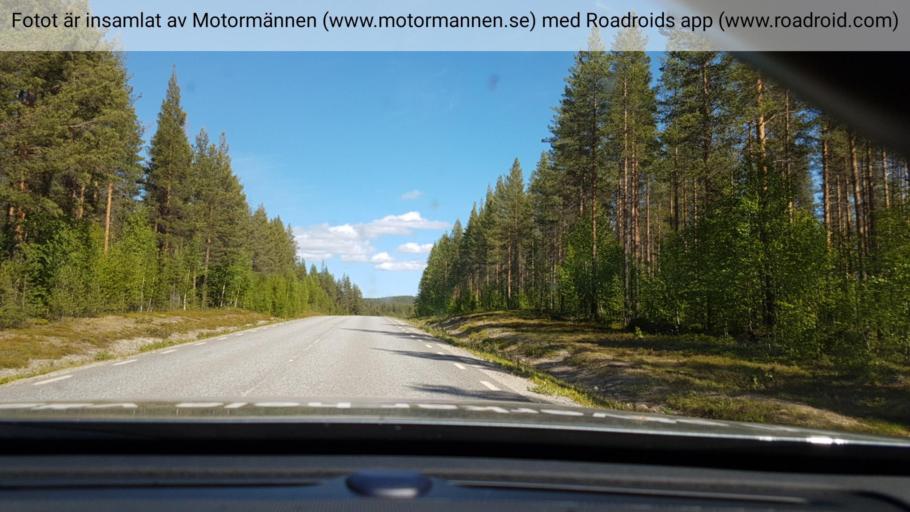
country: SE
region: Vaesterbotten
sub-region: Lycksele Kommun
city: Soderfors
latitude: 64.6207
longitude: 18.2819
